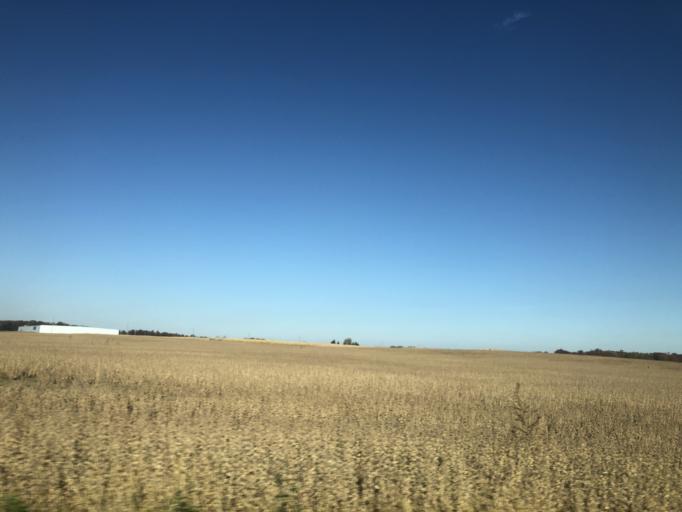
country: US
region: Indiana
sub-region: Allen County
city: Fort Wayne
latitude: 41.1111
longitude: -85.2223
